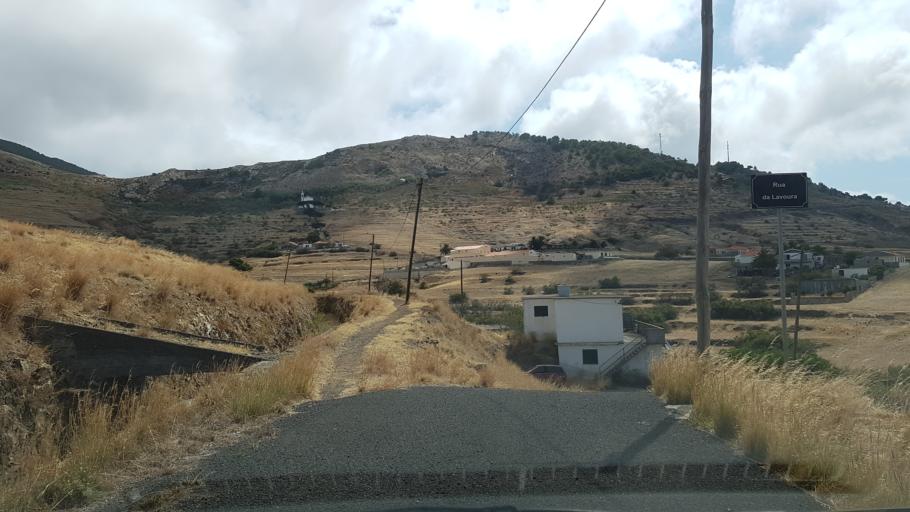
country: PT
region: Madeira
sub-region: Porto Santo
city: Vila de Porto Santo
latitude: 33.0701
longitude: -16.3301
